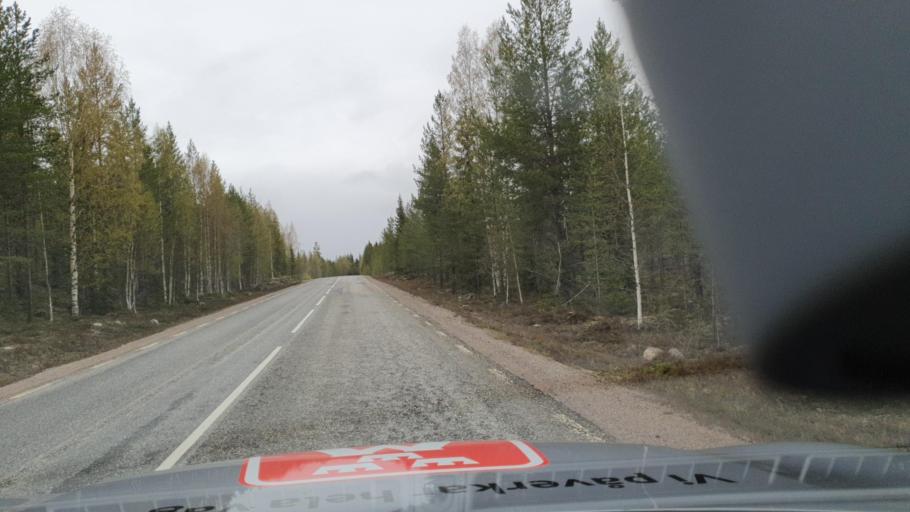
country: SE
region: Vaesternorrland
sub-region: Solleftea Kommun
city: Solleftea
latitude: 63.6654
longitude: 17.2590
